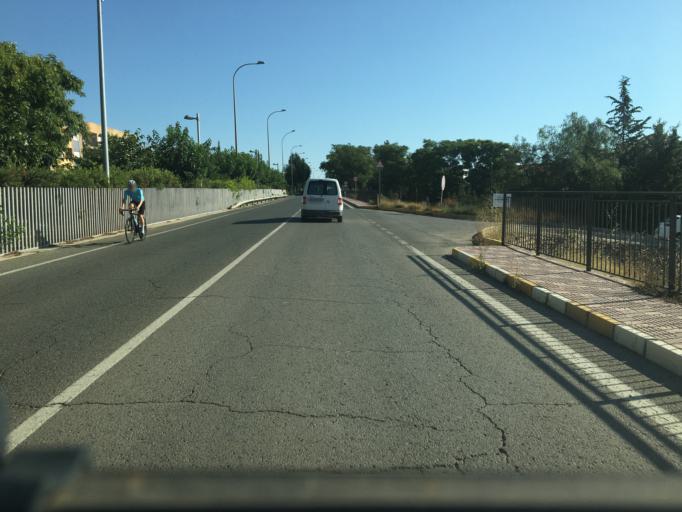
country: ES
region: Murcia
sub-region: Murcia
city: Puerto Lumbreras
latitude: 37.5567
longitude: -1.8099
